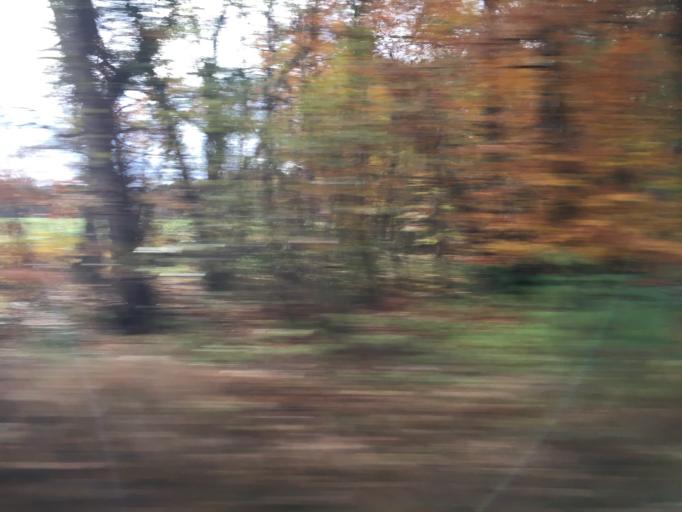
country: DE
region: North Rhine-Westphalia
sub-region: Regierungsbezirk Munster
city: Steinfurt
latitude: 52.1303
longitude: 7.3507
